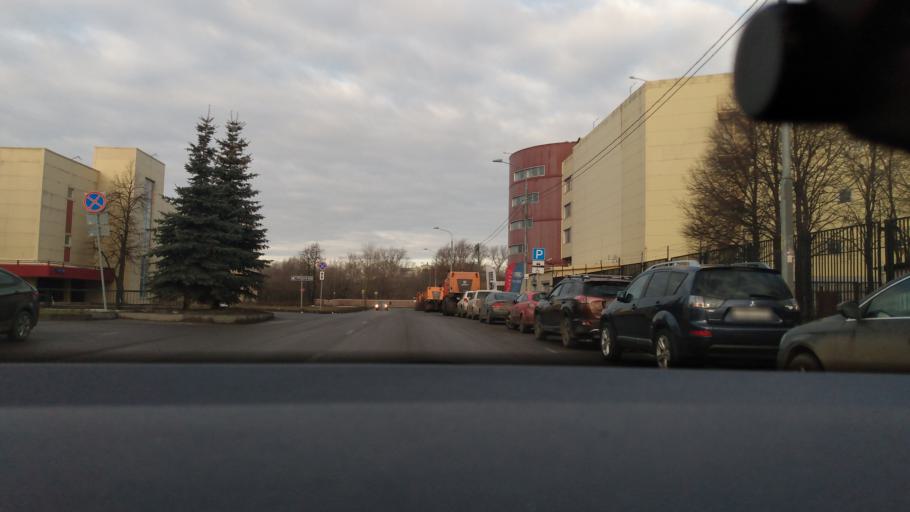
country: RU
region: Moscow
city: Strogino
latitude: 55.8254
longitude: 37.4208
